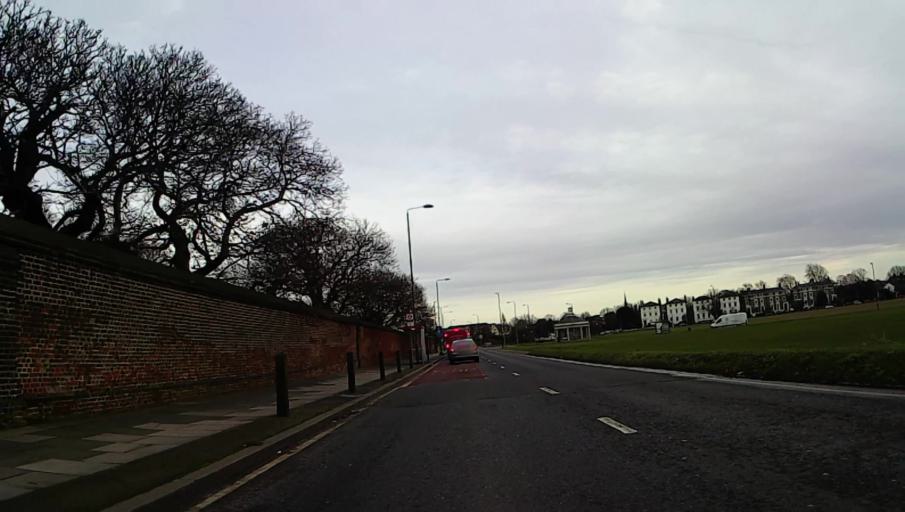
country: GB
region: England
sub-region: Greater London
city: Blackheath
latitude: 51.4745
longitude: 0.0084
